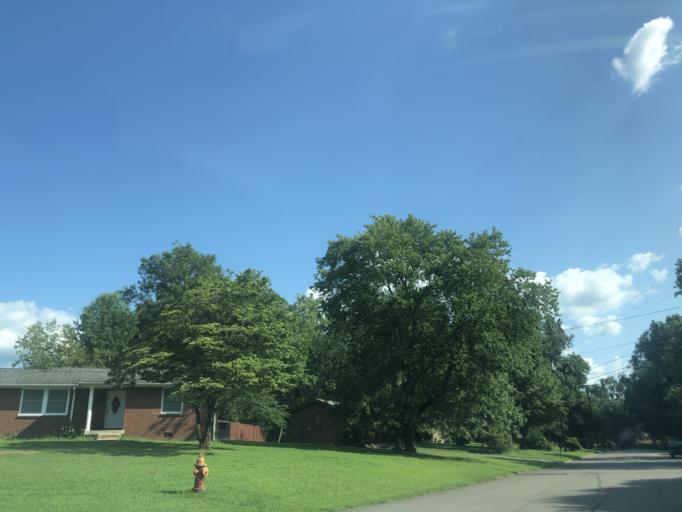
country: US
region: Tennessee
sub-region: Davidson County
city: Lakewood
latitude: 36.2089
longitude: -86.6004
